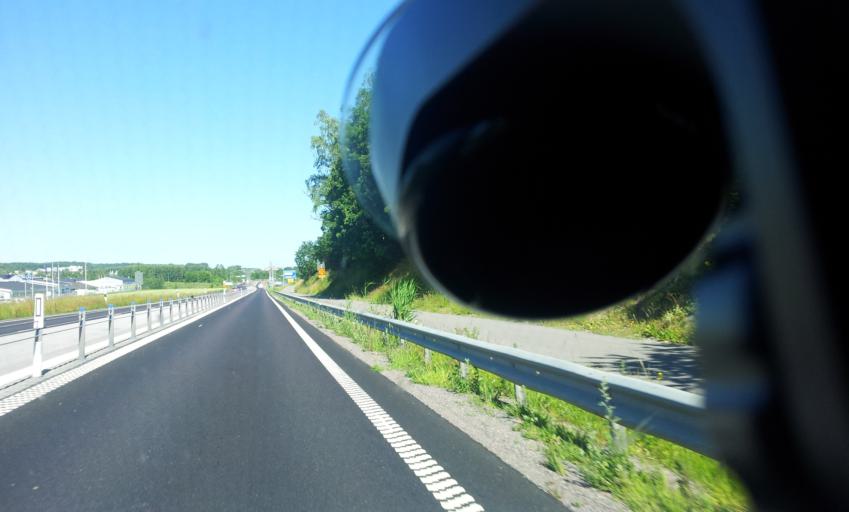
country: SE
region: OEstergoetland
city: Lindo
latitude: 58.5535
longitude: 16.2411
